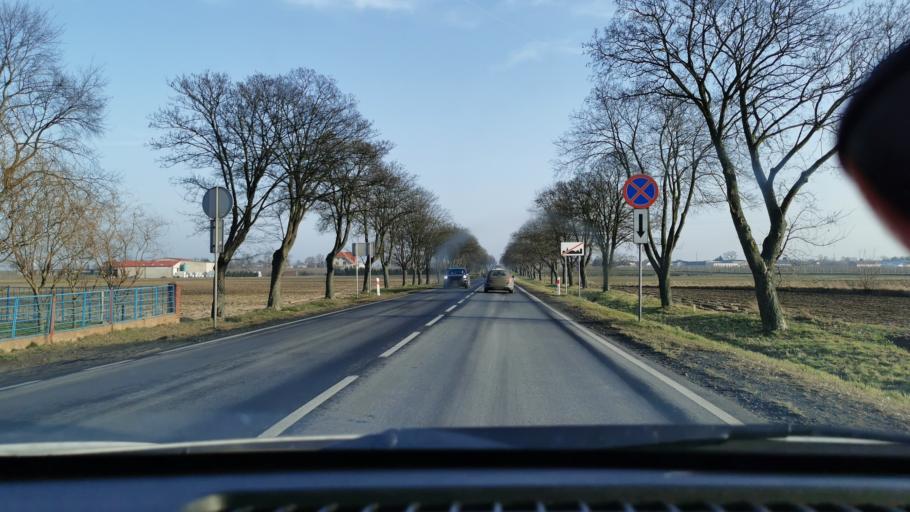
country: PL
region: Lodz Voivodeship
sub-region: Powiat sieradzki
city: Wroblew
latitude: 51.6287
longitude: 18.5567
